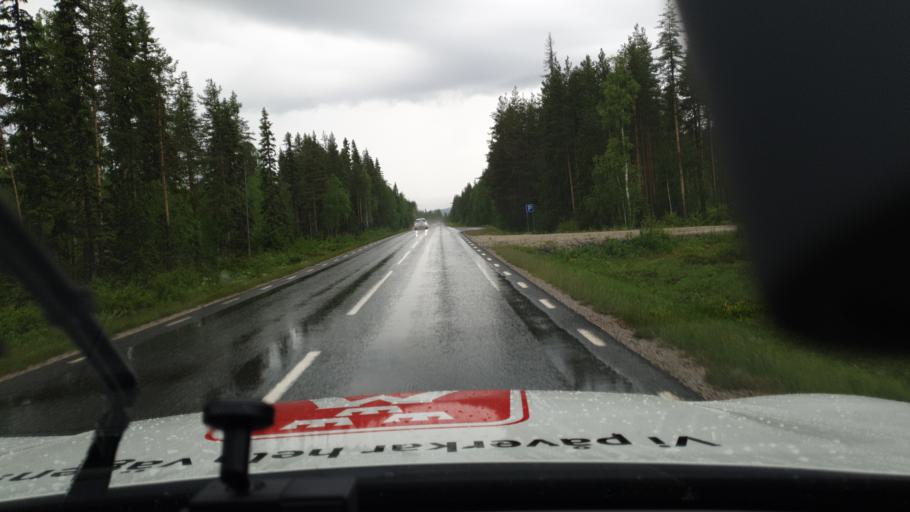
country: SE
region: Vaesterbotten
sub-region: Lycksele Kommun
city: Lycksele
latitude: 64.4605
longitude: 18.9035
